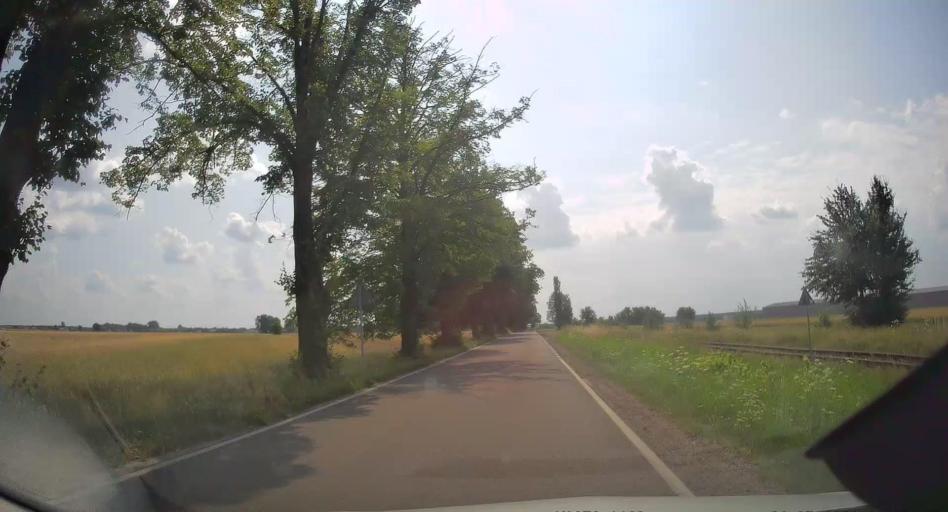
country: PL
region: Lodz Voivodeship
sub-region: Powiat tomaszowski
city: Lubochnia
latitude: 51.5723
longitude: 20.0978
